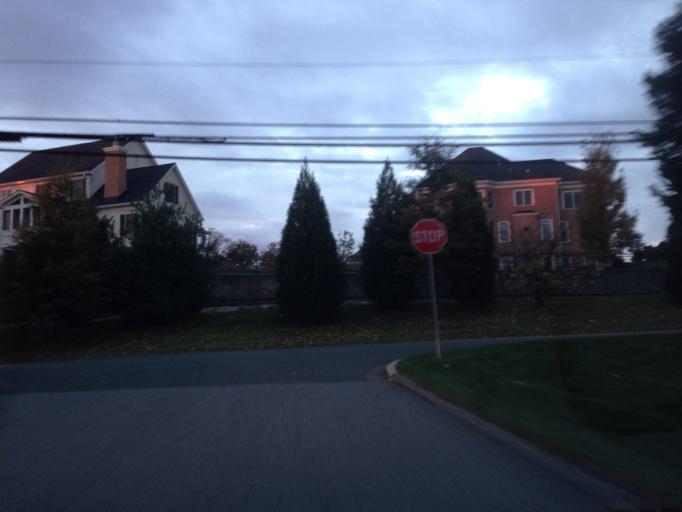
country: US
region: Maryland
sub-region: Baltimore County
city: Lutherville
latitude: 39.4109
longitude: -76.6336
